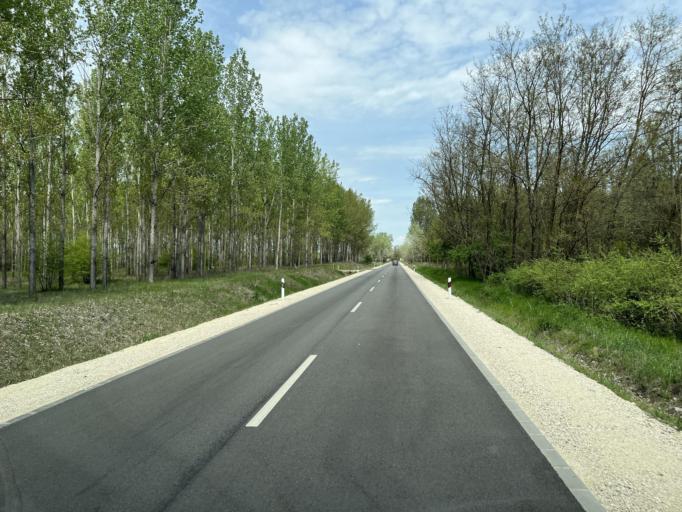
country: HU
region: Pest
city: Csemo
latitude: 47.1016
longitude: 19.6184
